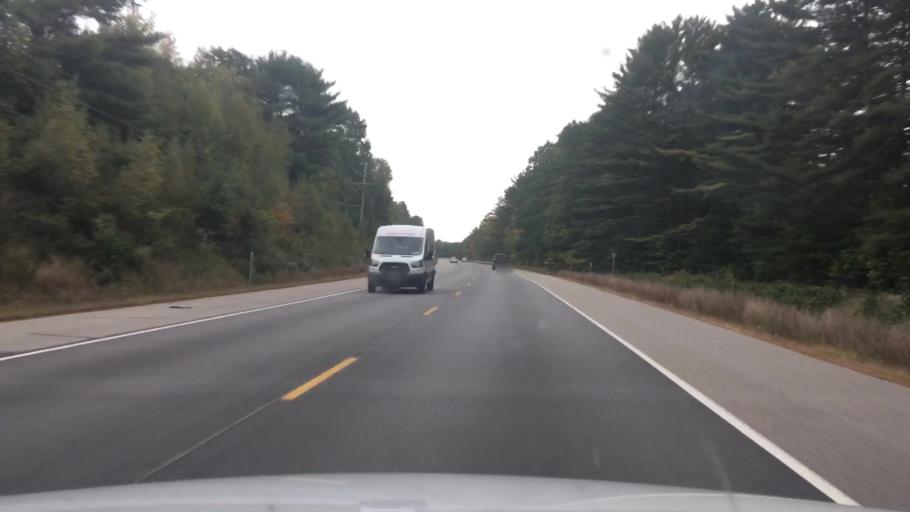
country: US
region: New Hampshire
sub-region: Strafford County
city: New Durham
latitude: 43.4422
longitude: -71.1968
